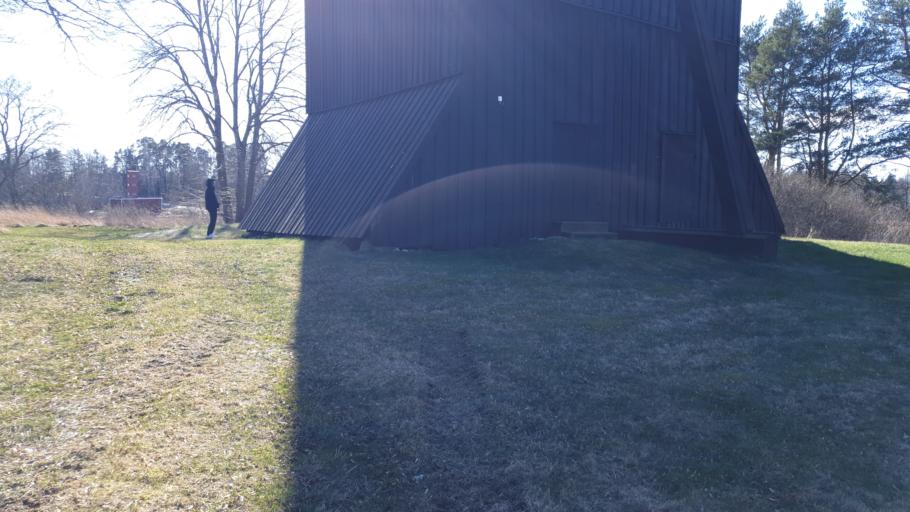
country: SE
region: Uppsala
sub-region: Enkopings Kommun
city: Dalby
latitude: 59.5212
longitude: 17.3217
